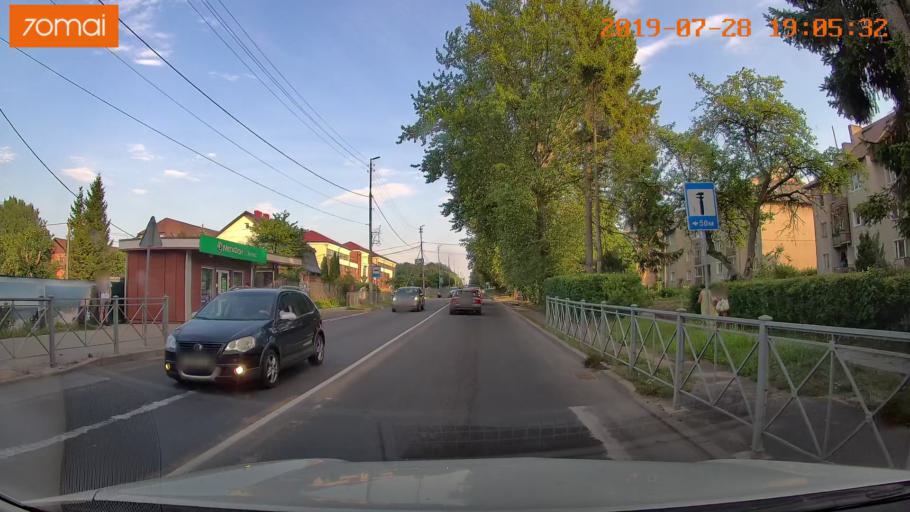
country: RU
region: Kaliningrad
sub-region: Gorod Svetlogorsk
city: Svetlogorsk
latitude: 54.9325
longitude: 20.1633
